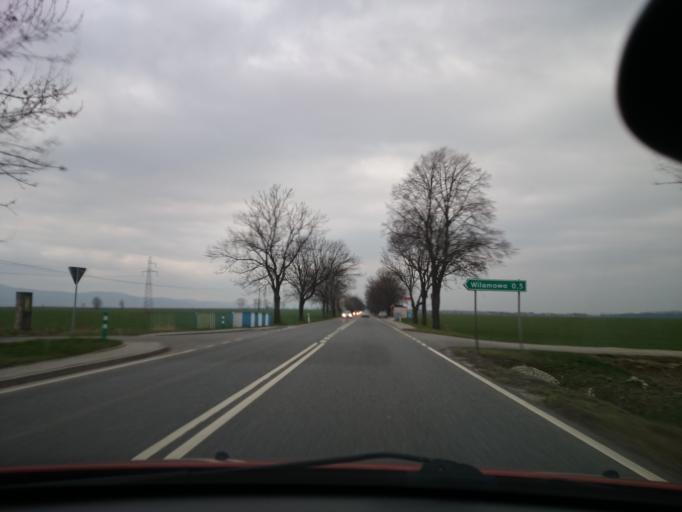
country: PL
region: Opole Voivodeship
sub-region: Powiat nyski
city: Paczkow
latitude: 50.4498
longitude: 17.0816
